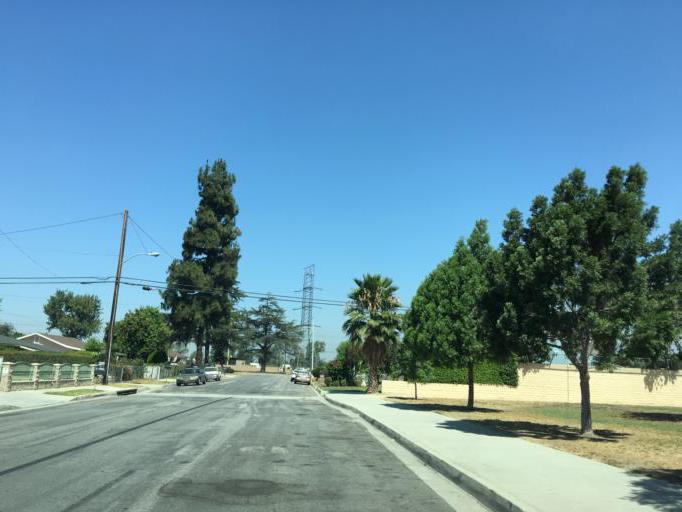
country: US
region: California
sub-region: Los Angeles County
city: Avocado Heights
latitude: 34.0493
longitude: -118.0036
